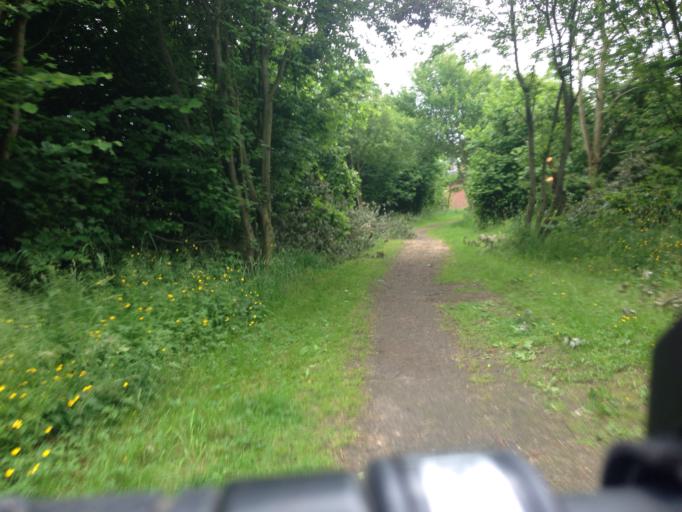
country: DE
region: Schleswig-Holstein
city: Barsbuettel
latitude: 53.5878
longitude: 10.1669
